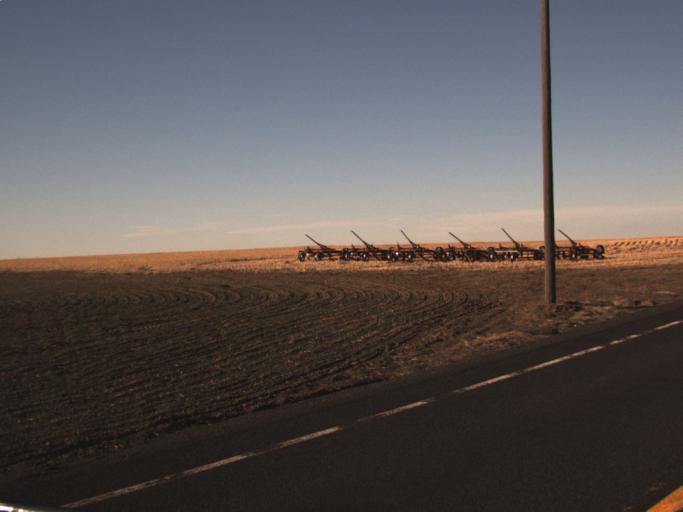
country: US
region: Washington
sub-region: Adams County
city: Ritzville
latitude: 46.8880
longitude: -118.3343
